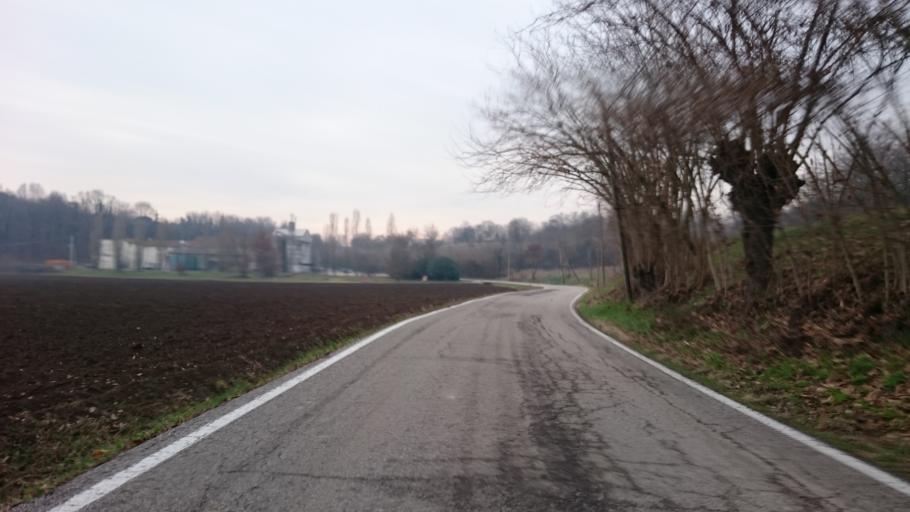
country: IT
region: Veneto
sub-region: Provincia di Vicenza
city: Montegalda
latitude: 45.4575
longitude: 11.6676
